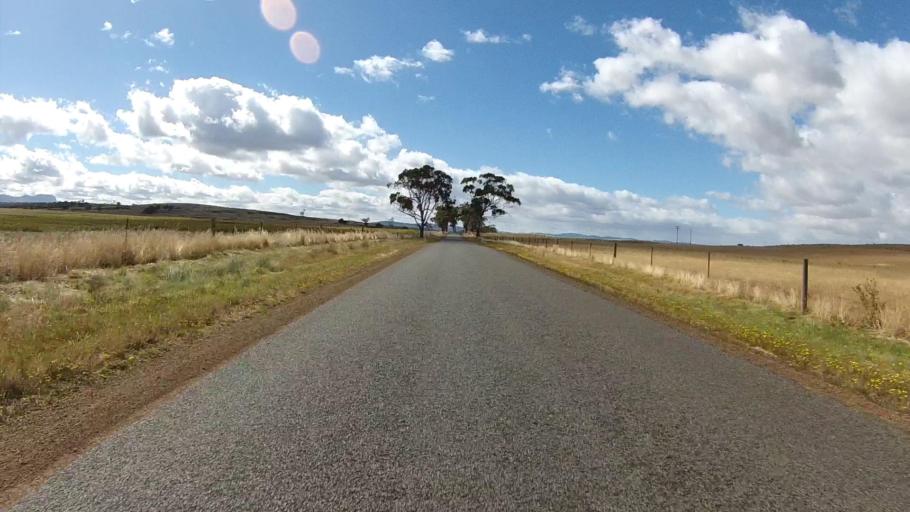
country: AU
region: Tasmania
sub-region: Northern Midlands
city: Evandale
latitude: -41.7006
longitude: 147.3785
